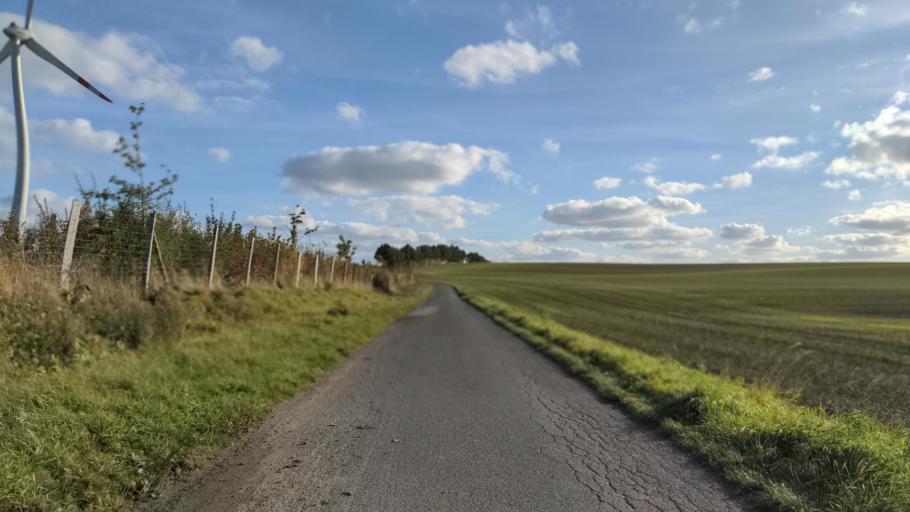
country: DE
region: Schleswig-Holstein
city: Schashagen
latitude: 54.1450
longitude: 10.9028
